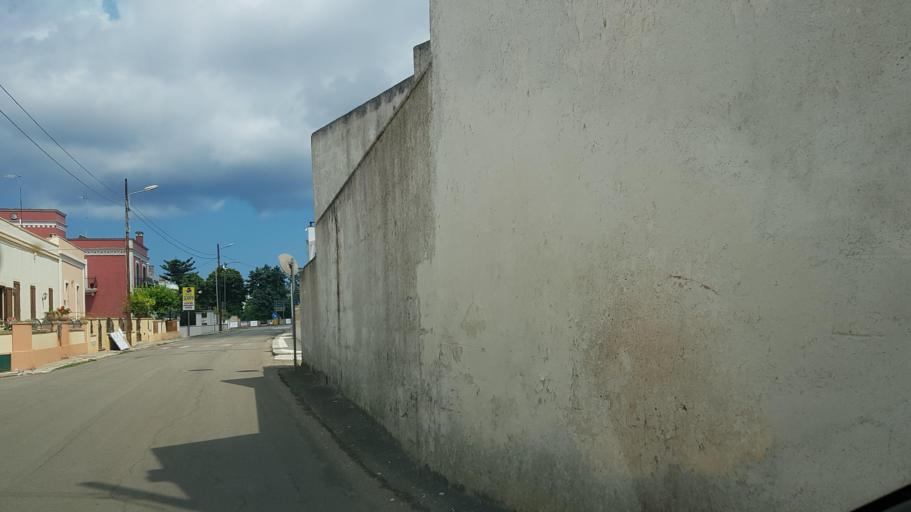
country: IT
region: Apulia
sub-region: Provincia di Lecce
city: Patu
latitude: 39.8434
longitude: 18.3369
